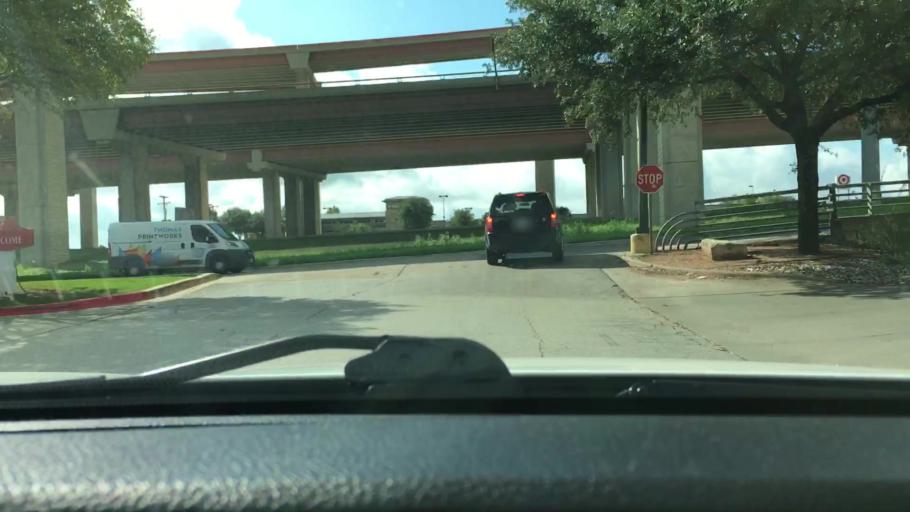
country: US
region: Texas
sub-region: Williamson County
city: Round Rock
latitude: 30.4813
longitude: -97.6722
